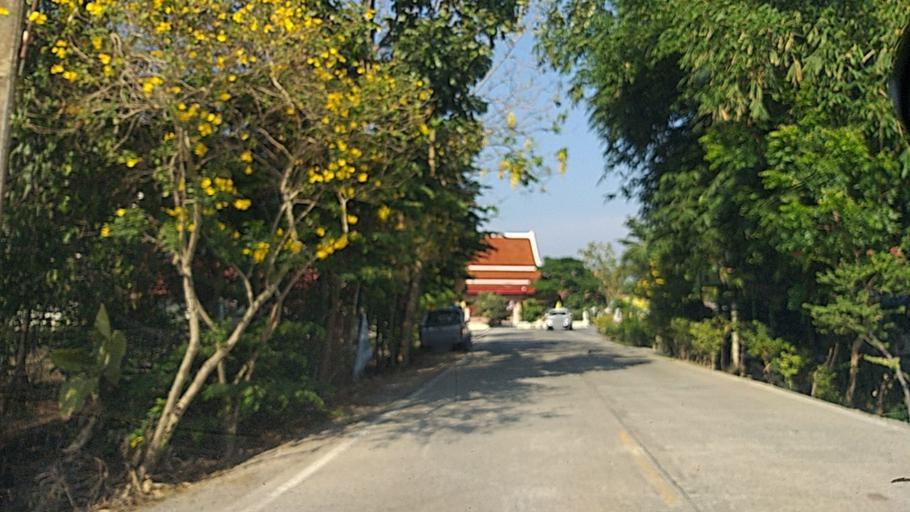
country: TH
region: Nonthaburi
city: Sai Noi
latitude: 13.9426
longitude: 100.3293
